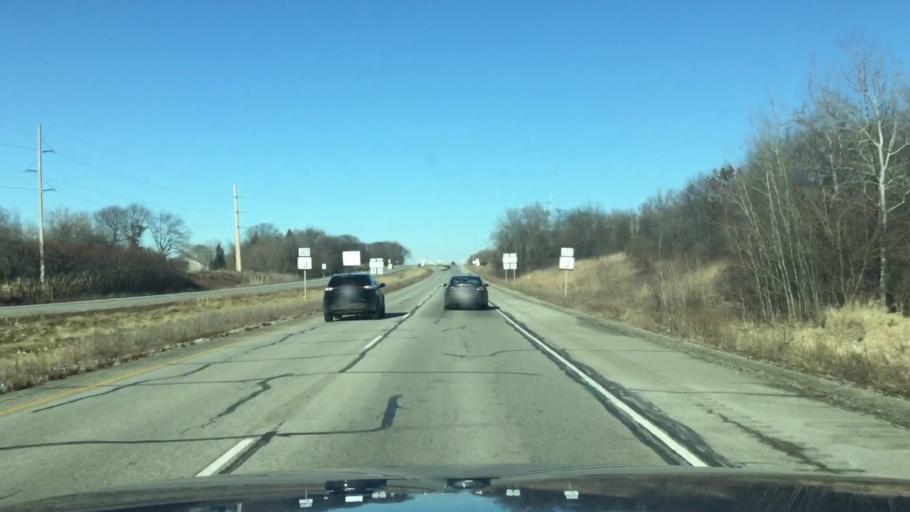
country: US
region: Wisconsin
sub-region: Racine County
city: Rochester
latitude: 42.7321
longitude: -88.2194
